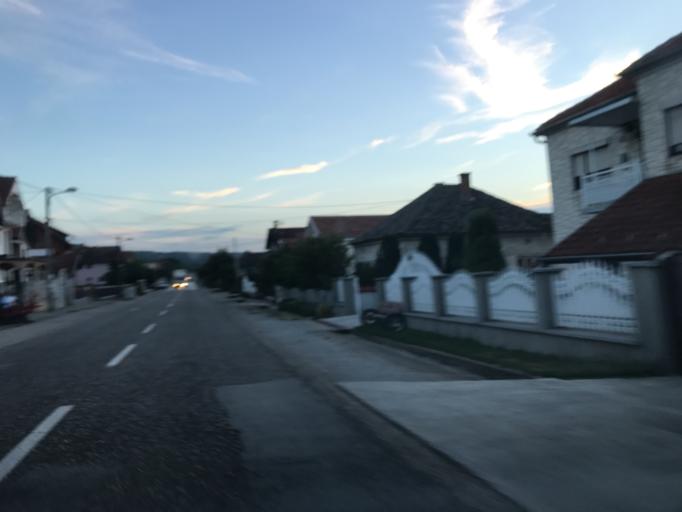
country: RS
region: Central Serbia
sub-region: Branicevski Okrug
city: Veliko Gradiste
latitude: 44.7300
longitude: 21.4653
